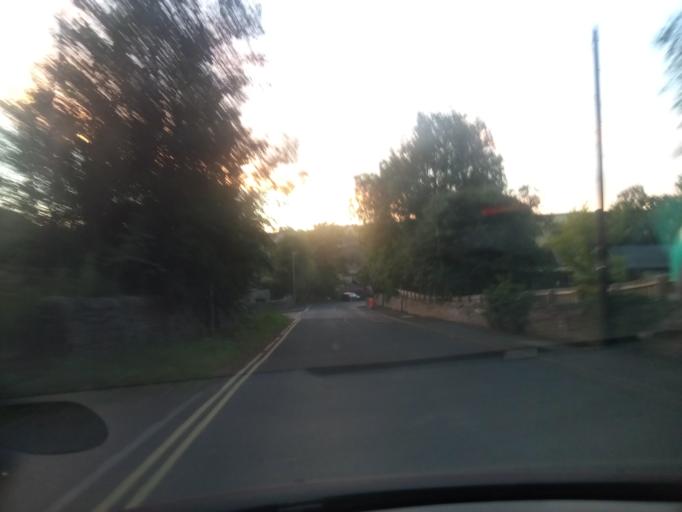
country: GB
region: England
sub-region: Northumberland
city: Bardon Mill
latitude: 54.9702
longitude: -2.2467
